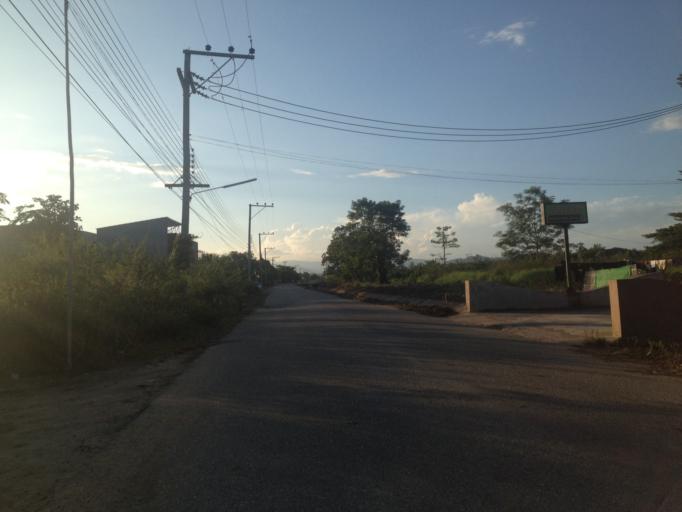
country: TH
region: Chiang Mai
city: San Pa Tong
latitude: 18.6458
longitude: 98.8991
